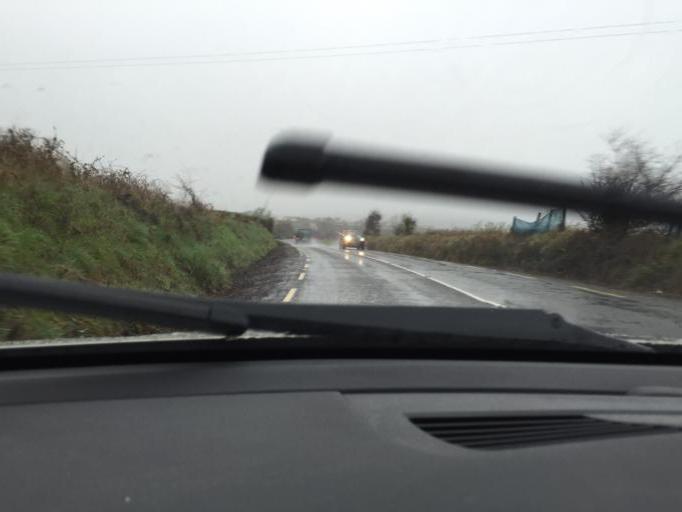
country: IE
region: Munster
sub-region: Ciarrai
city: Dingle
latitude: 52.1335
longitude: -10.3044
